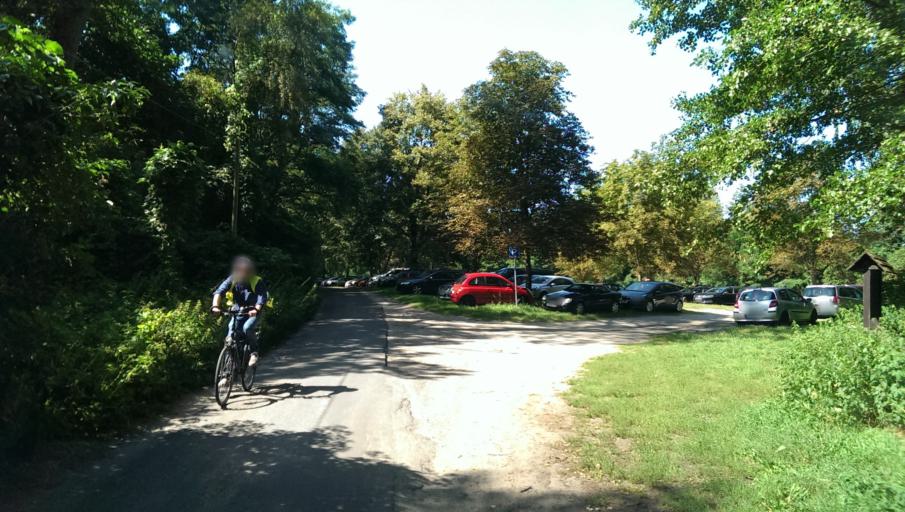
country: DE
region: Brandenburg
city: Michendorf
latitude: 52.2709
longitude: 13.0538
